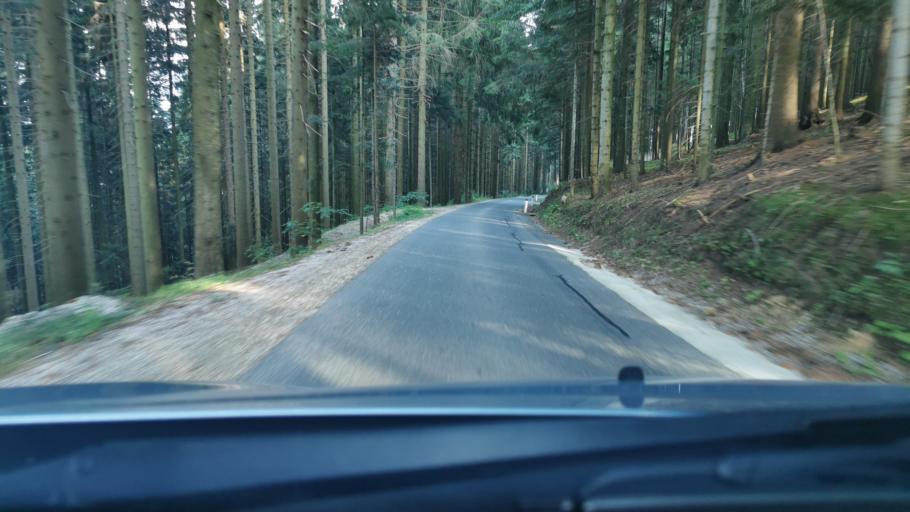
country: AT
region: Styria
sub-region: Politischer Bezirk Weiz
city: Fischbach
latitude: 47.3903
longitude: 15.6391
